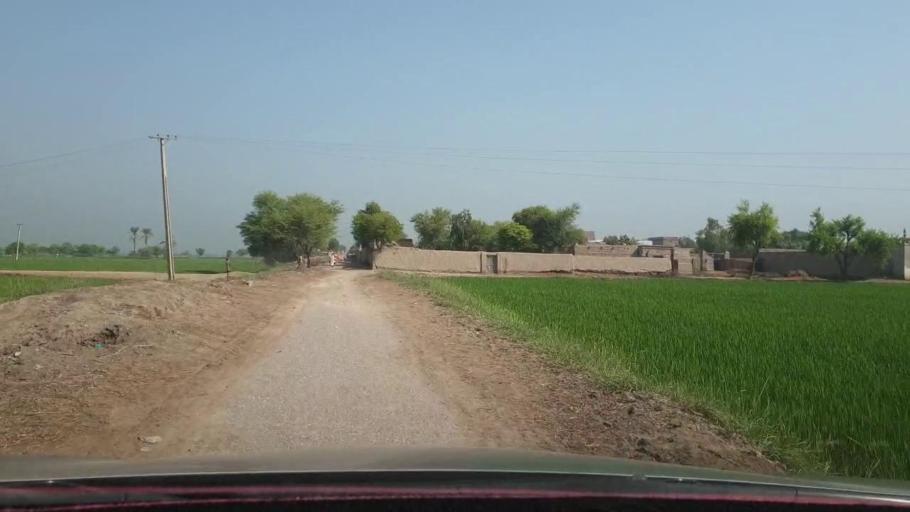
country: PK
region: Sindh
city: Kambar
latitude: 27.6012
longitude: 67.9362
